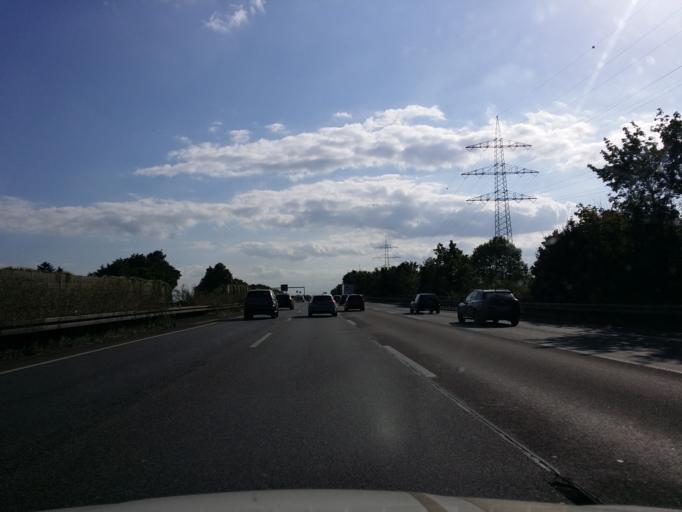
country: DE
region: Hesse
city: Sulzbach
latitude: 50.1129
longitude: 8.5264
